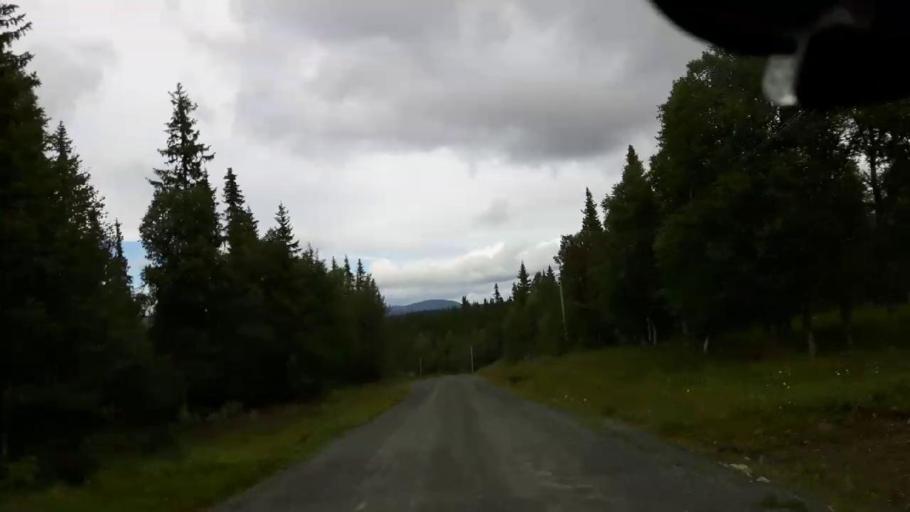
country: SE
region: Jaemtland
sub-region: Krokoms Kommun
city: Valla
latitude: 63.7770
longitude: 13.8296
